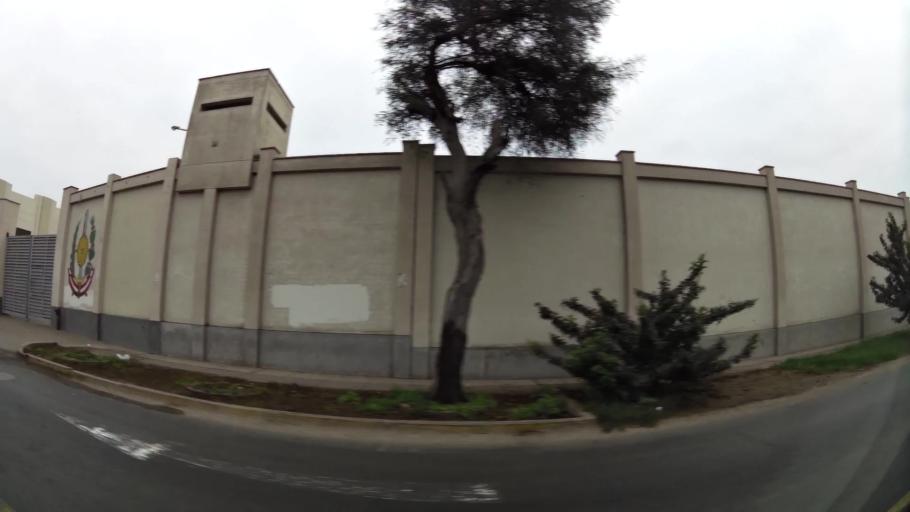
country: PE
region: Callao
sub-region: Callao
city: Callao
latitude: -12.0743
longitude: -77.1187
